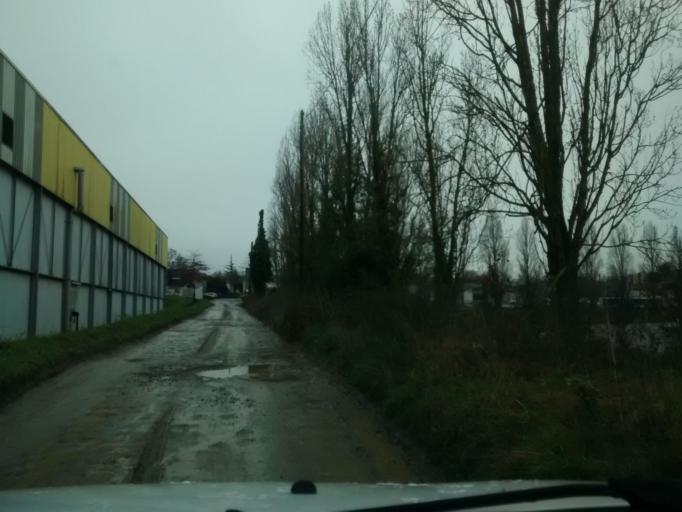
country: FR
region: Brittany
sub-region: Departement d'Ille-et-Vilaine
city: Chantepie
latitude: 48.1074
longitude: -1.6250
